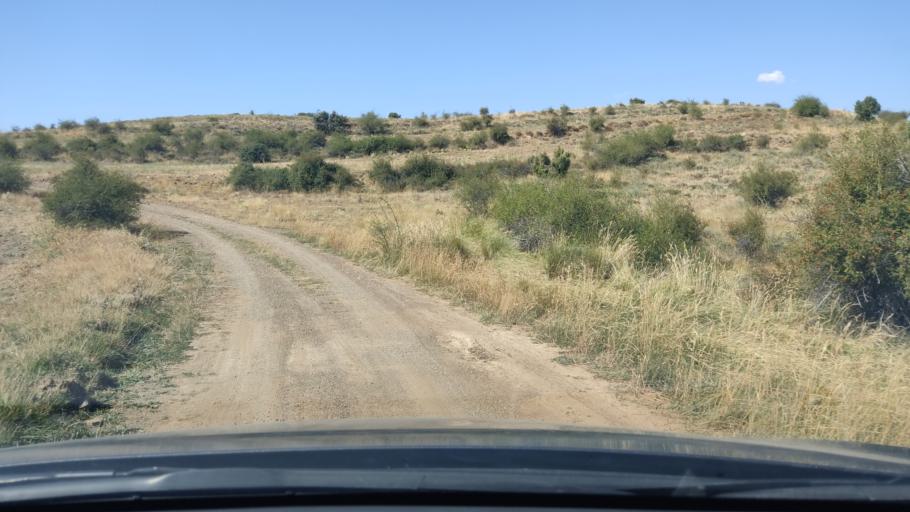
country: ES
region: Aragon
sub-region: Provincia de Teruel
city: Montalban
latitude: 40.8771
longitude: -0.8250
